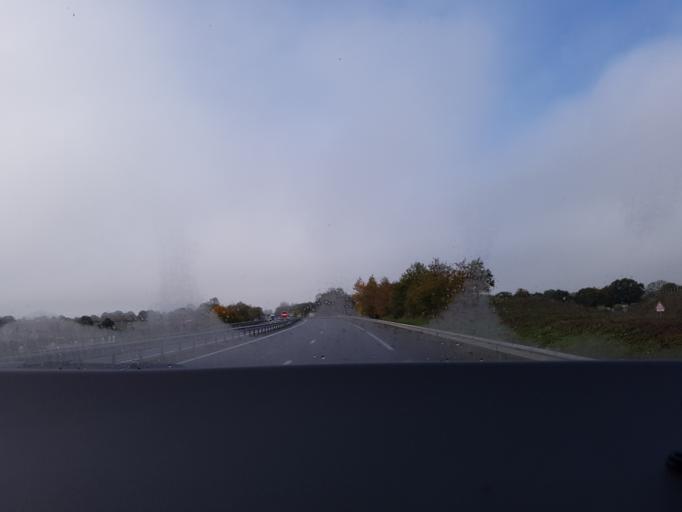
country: FR
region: Poitou-Charentes
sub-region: Departement des Deux-Sevres
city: Bressuire
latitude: 46.8575
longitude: -0.5125
